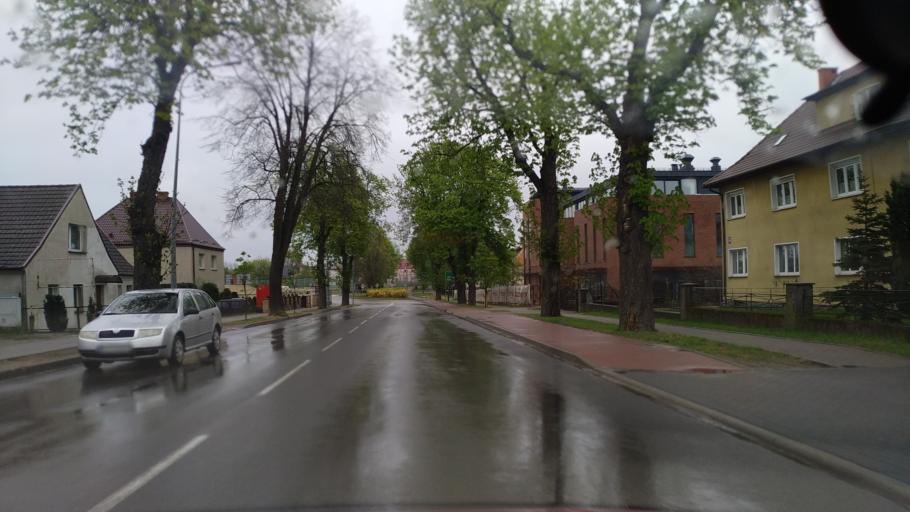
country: PL
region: Pomeranian Voivodeship
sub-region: Powiat czluchowski
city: Czluchow
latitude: 53.6718
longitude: 17.3672
